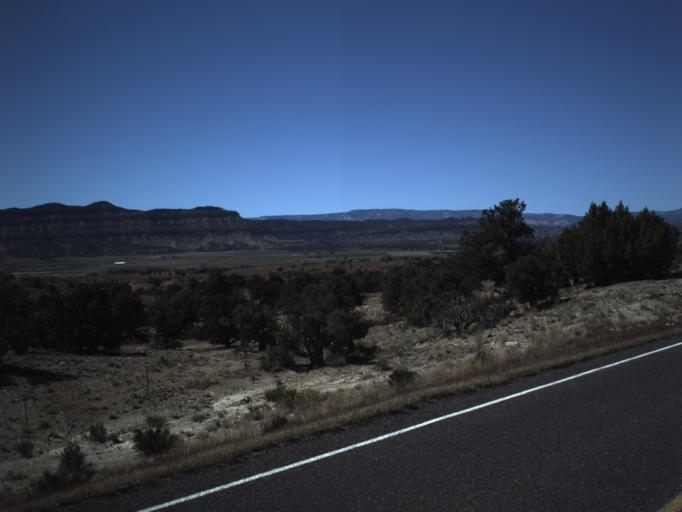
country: US
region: Utah
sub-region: Wayne County
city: Loa
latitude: 37.7352
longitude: -111.5431
